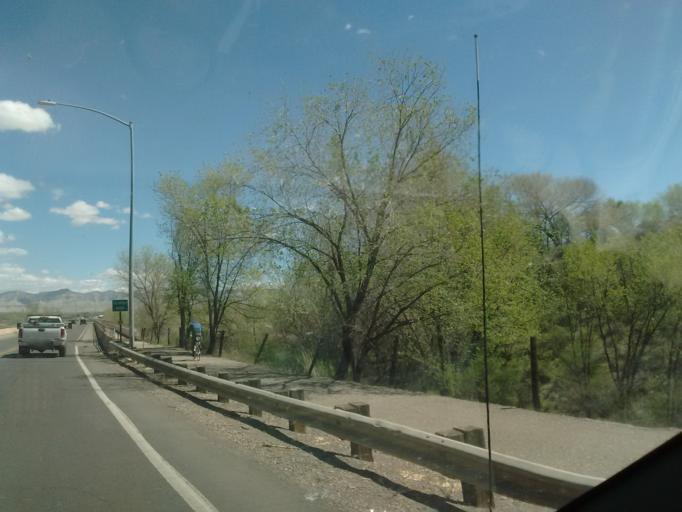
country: US
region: Colorado
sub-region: Mesa County
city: Redlands
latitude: 39.0873
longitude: -108.6262
